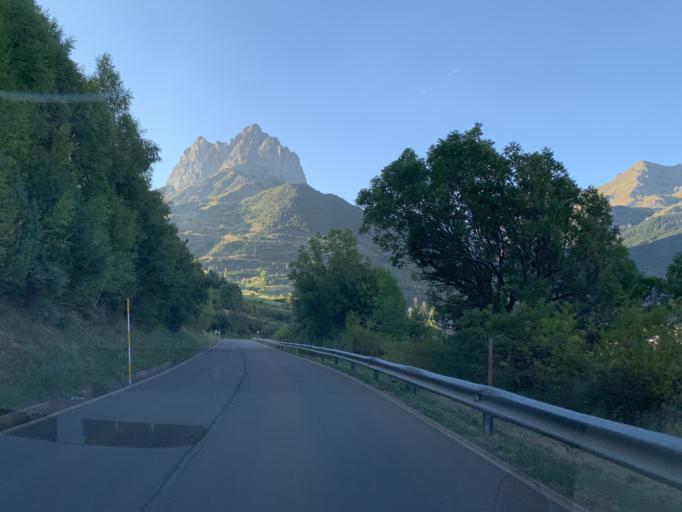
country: ES
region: Aragon
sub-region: Provincia de Huesca
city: Sallent de Gallego
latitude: 42.7639
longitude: -0.3359
